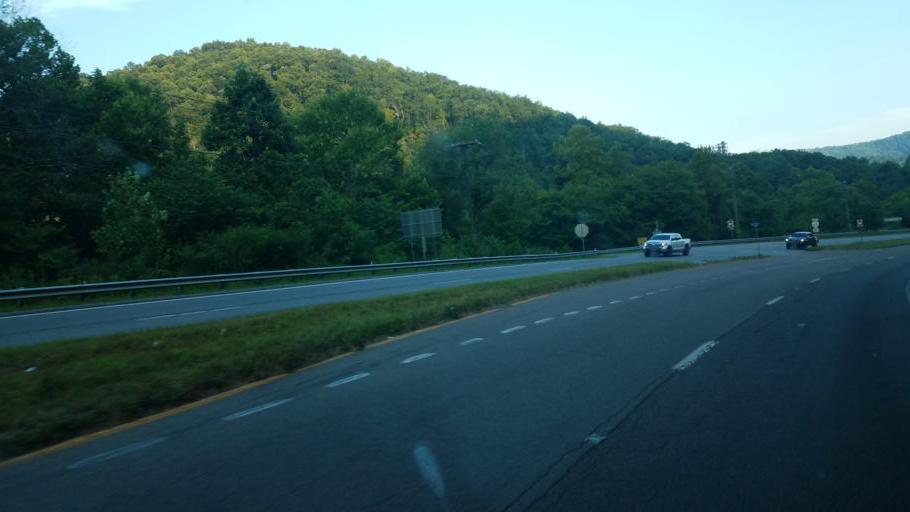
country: US
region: Tennessee
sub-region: Hawkins County
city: Church Hill
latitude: 36.6695
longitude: -82.7531
